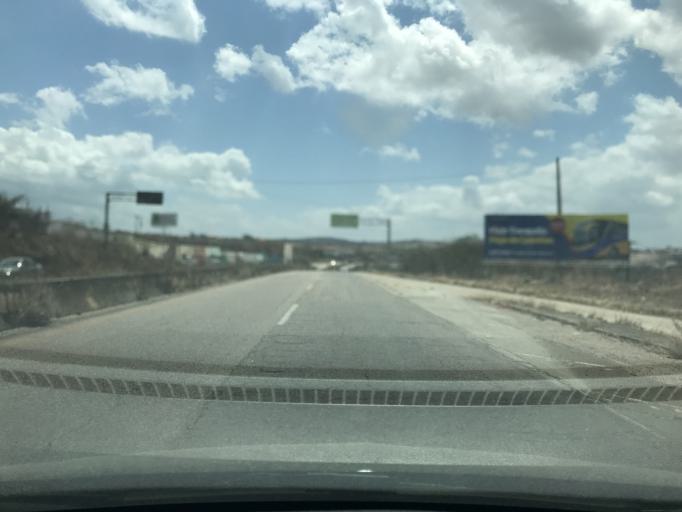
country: BR
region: Pernambuco
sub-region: Caruaru
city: Caruaru
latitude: -8.3081
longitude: -35.9456
